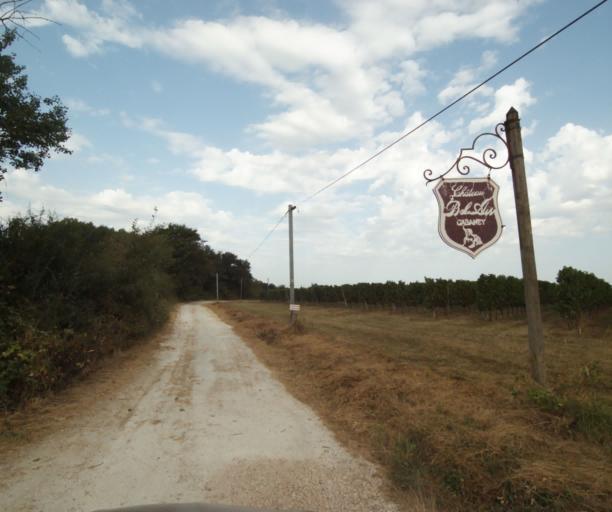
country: FR
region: Aquitaine
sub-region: Departement de la Gironde
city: Creon
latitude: 44.7715
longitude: -0.3642
